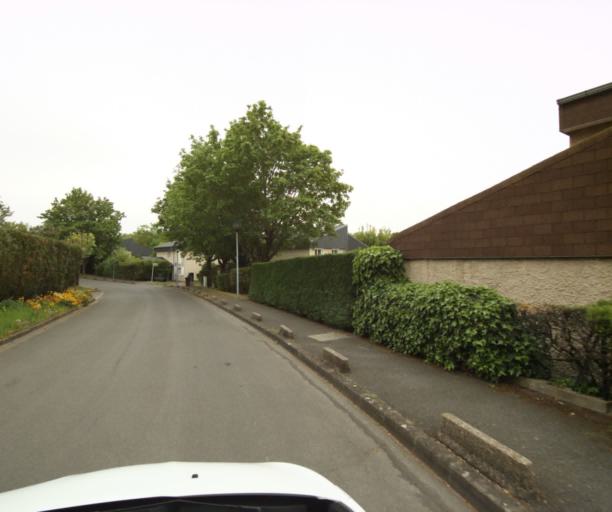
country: FR
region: Ile-de-France
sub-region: Departement de Seine-et-Marne
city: Noisiel
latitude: 48.8497
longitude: 2.6342
